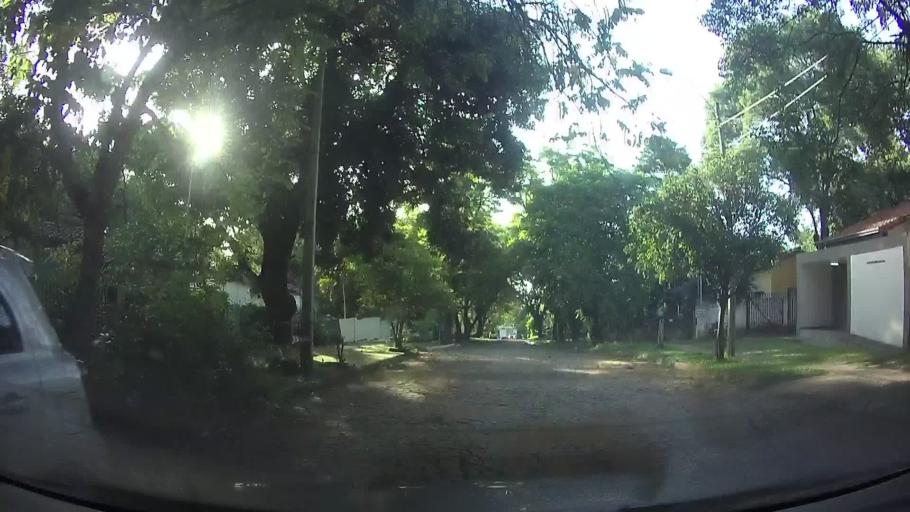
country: PY
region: Asuncion
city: Asuncion
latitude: -25.2739
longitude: -57.5830
